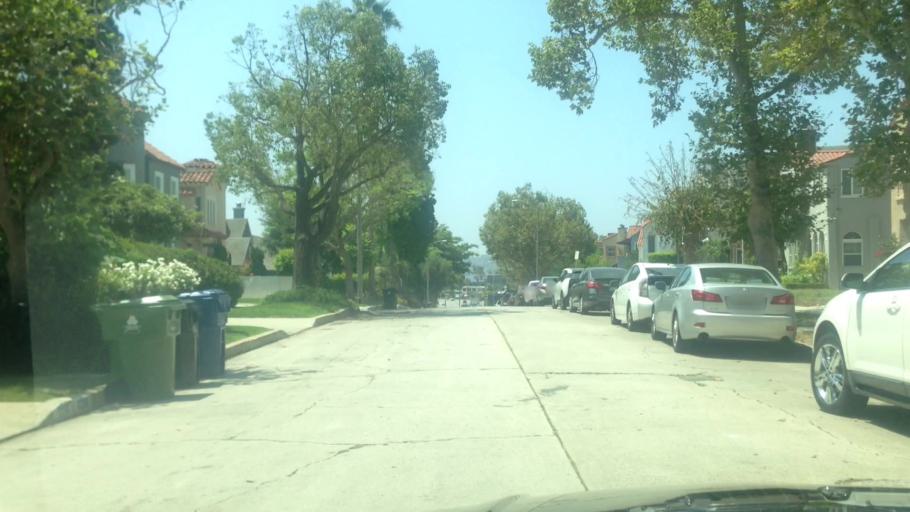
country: US
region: California
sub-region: Los Angeles County
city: West Hollywood
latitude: 34.0562
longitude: -118.3426
